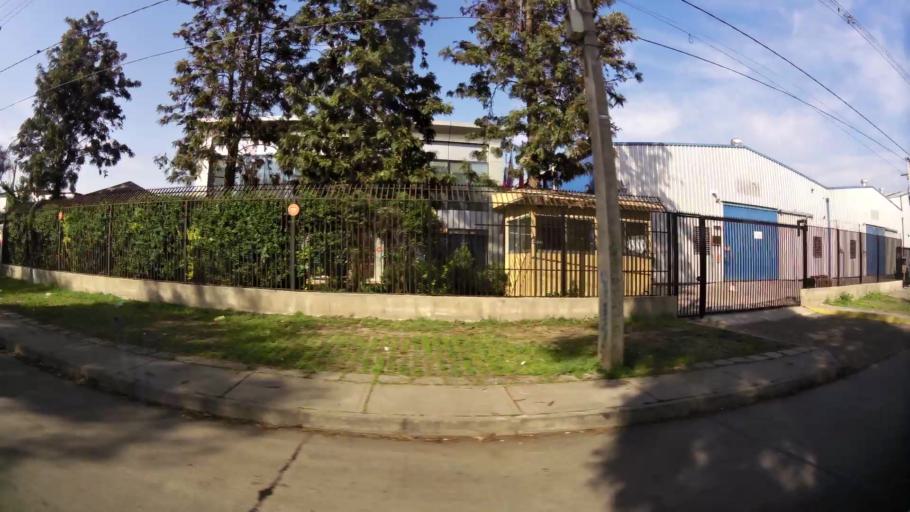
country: CL
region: Santiago Metropolitan
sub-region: Provincia de Santiago
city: Lo Prado
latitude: -33.4540
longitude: -70.7515
